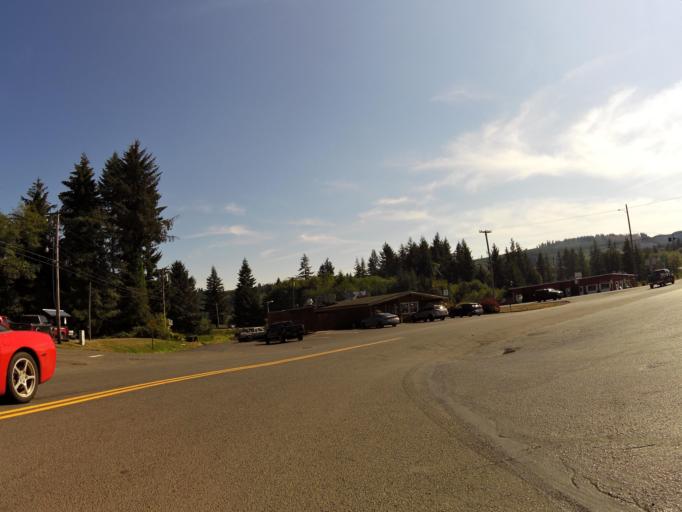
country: US
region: Washington
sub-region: Wahkiakum County
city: Cathlamet
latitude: 46.1688
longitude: -123.5821
